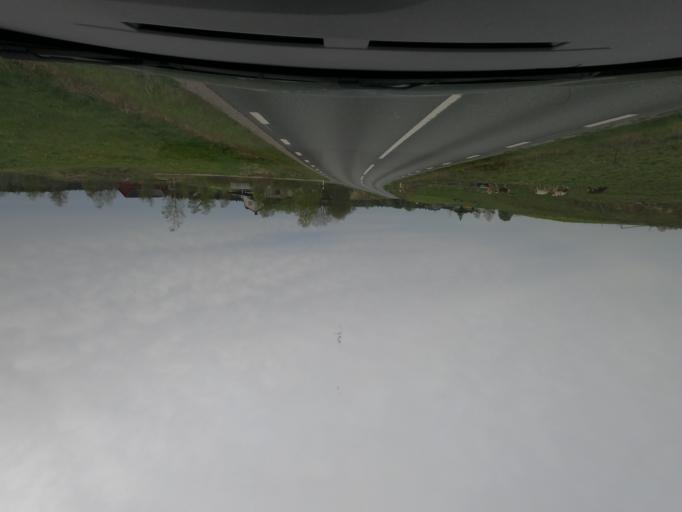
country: SE
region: Joenkoeping
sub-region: Varnamo Kommun
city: Bredaryd
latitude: 57.2033
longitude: 13.7624
